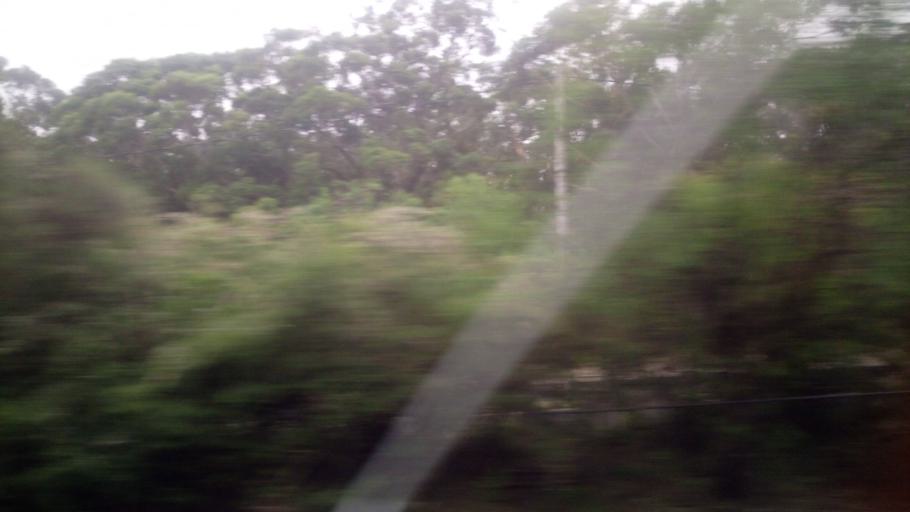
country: AU
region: New South Wales
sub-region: Blue Mountains Municipality
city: Lawson
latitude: -33.7253
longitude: 150.3874
